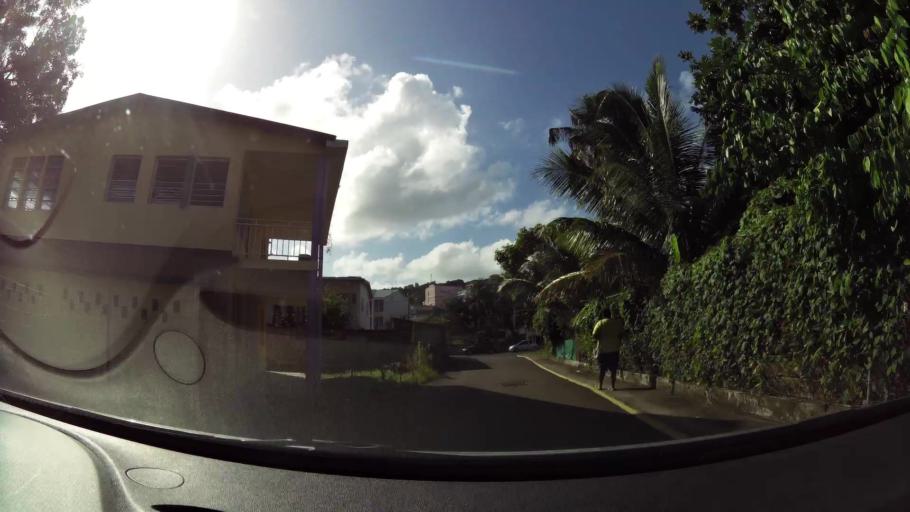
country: MQ
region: Martinique
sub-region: Martinique
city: La Trinite
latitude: 14.7383
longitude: -60.9646
